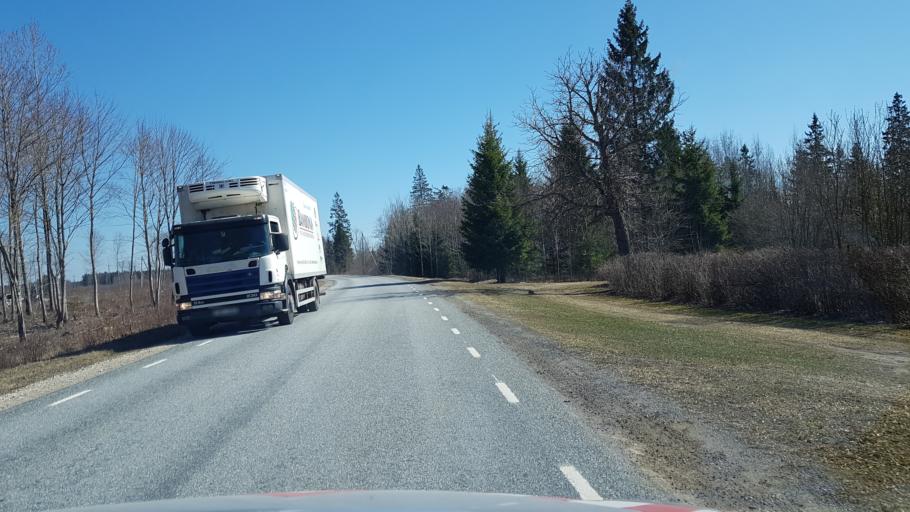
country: EE
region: Laeaene-Virumaa
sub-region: Vaeike-Maarja vald
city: Vaike-Maarja
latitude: 59.1264
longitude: 26.2766
